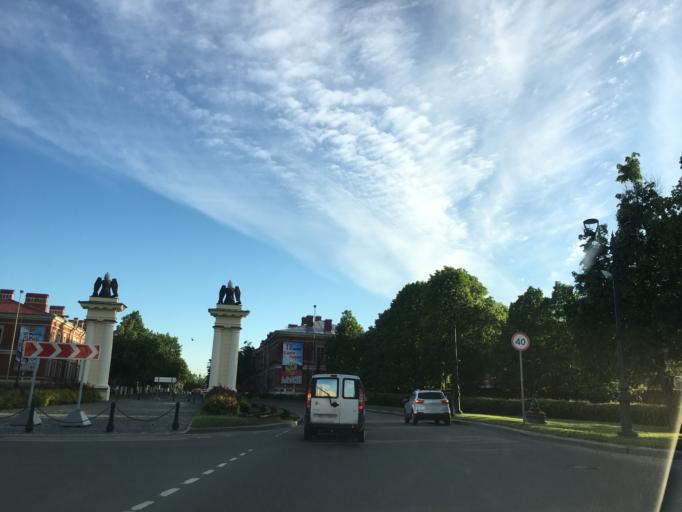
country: RU
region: Leningrad
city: Gatchina
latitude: 59.5769
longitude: 30.1325
